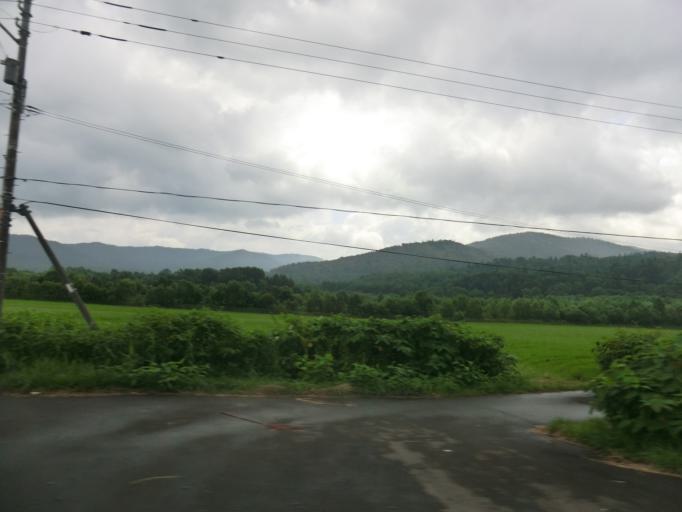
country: JP
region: Hokkaido
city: Nayoro
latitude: 44.1184
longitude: 142.1407
